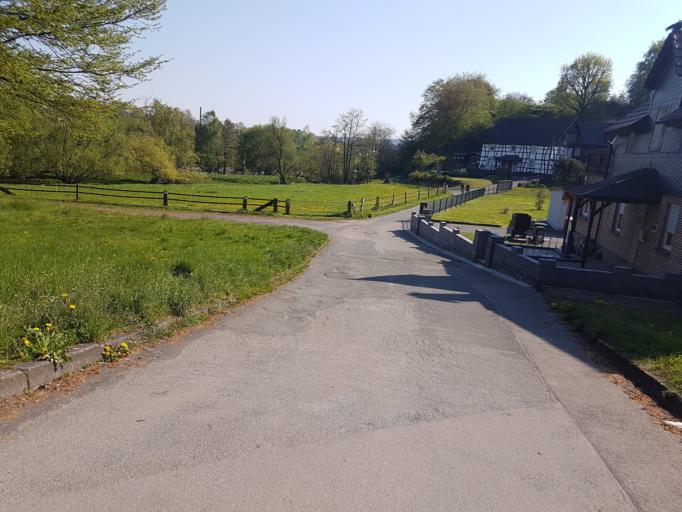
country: DE
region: North Rhine-Westphalia
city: Hattingen
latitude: 51.4192
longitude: 7.1844
